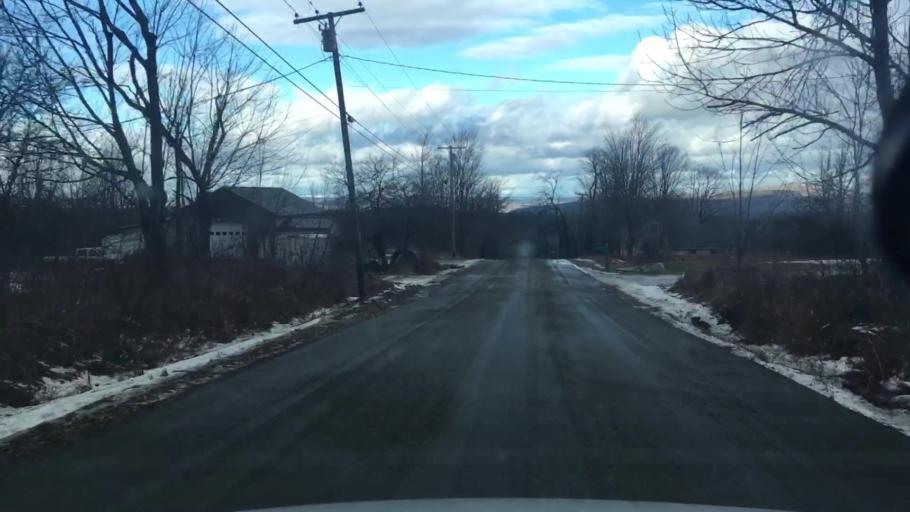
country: US
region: Maine
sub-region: Penobscot County
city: Orrington
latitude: 44.6814
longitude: -68.7551
